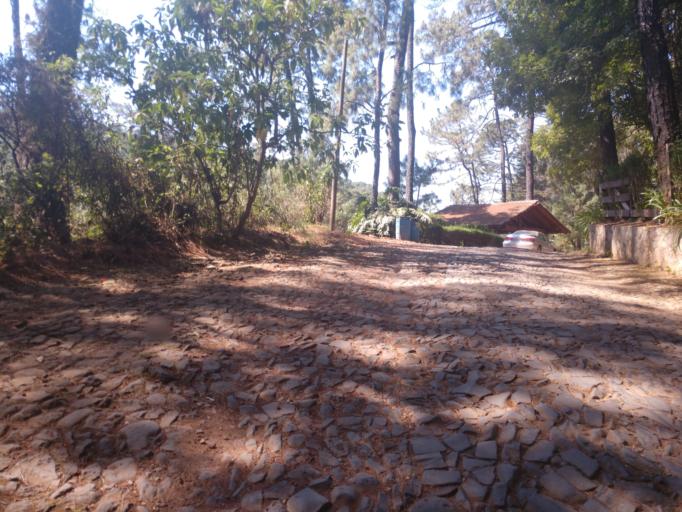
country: MX
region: Jalisco
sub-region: Mazamitla
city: Mazamitla
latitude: 19.9018
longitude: -103.0329
